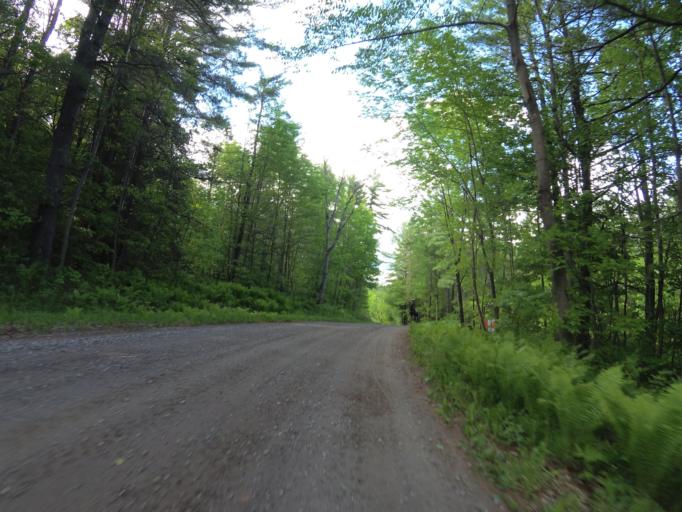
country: CA
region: Ontario
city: Renfrew
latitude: 45.1833
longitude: -76.8941
